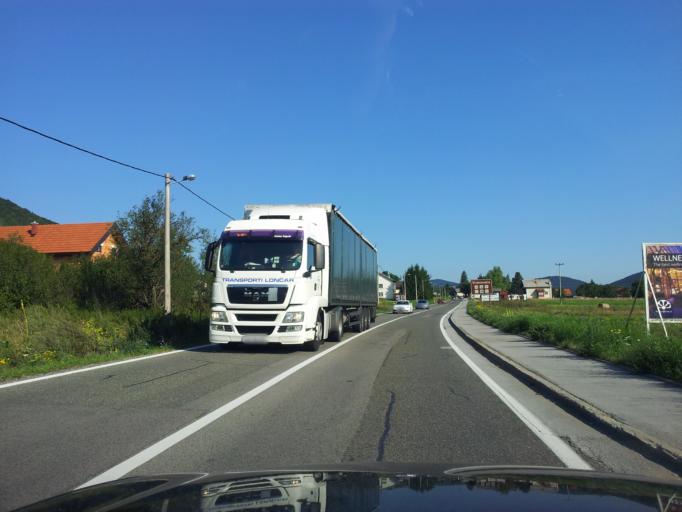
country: BA
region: Federation of Bosnia and Herzegovina
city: Izacic
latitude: 44.7525
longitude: 15.7016
